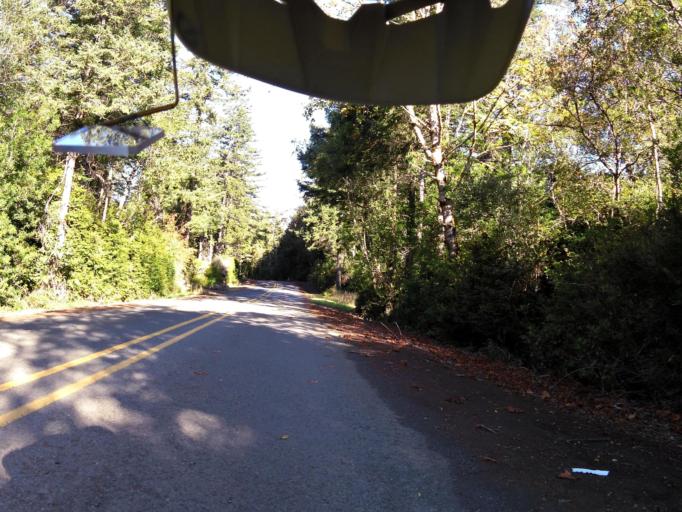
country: US
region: Oregon
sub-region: Coos County
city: Bandon
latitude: 43.0356
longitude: -124.3911
